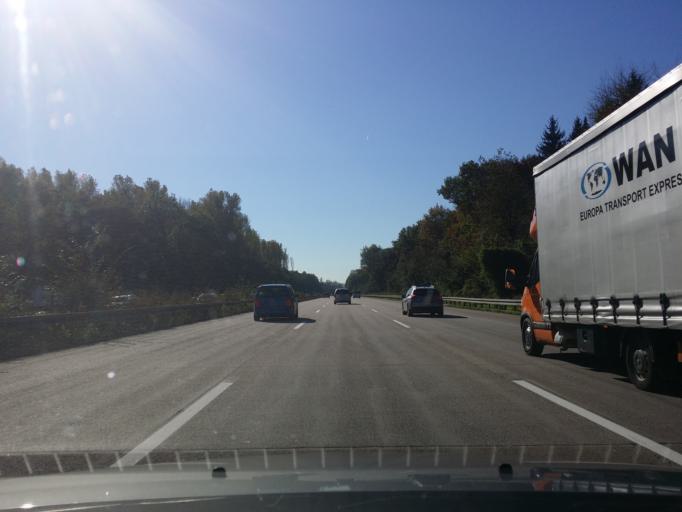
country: DE
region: Baden-Wuerttemberg
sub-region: Karlsruhe Region
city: Weingarten
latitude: 49.0393
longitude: 8.4868
